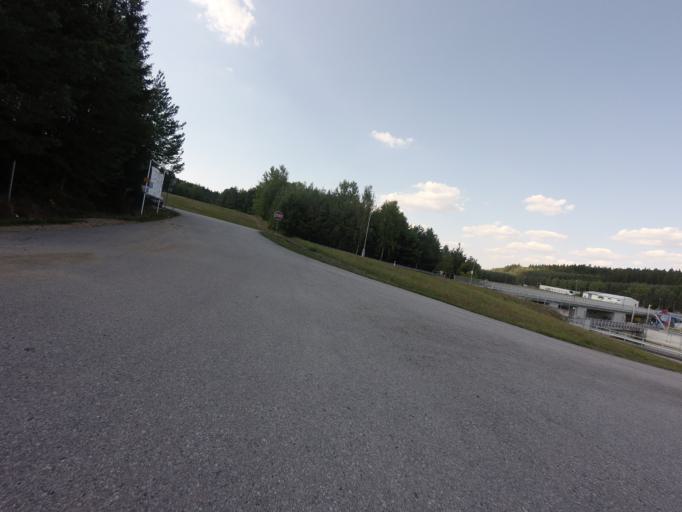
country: CZ
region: Jihocesky
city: Tyn nad Vltavou
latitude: 49.1805
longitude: 14.4448
